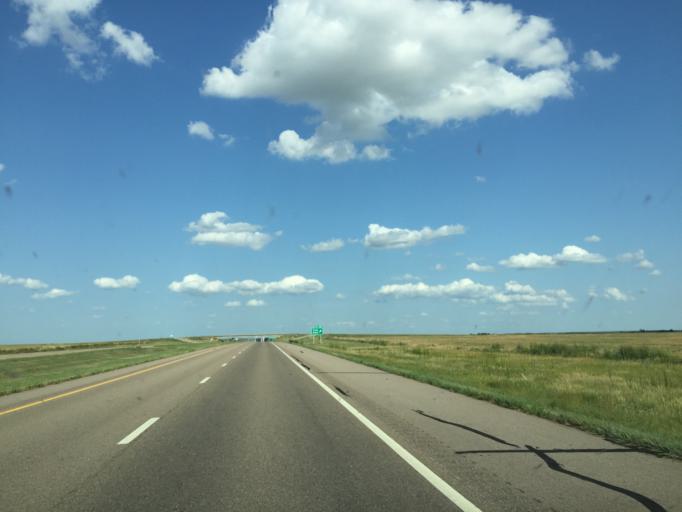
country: US
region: Kansas
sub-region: Trego County
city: WaKeeney
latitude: 39.0230
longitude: -100.0275
